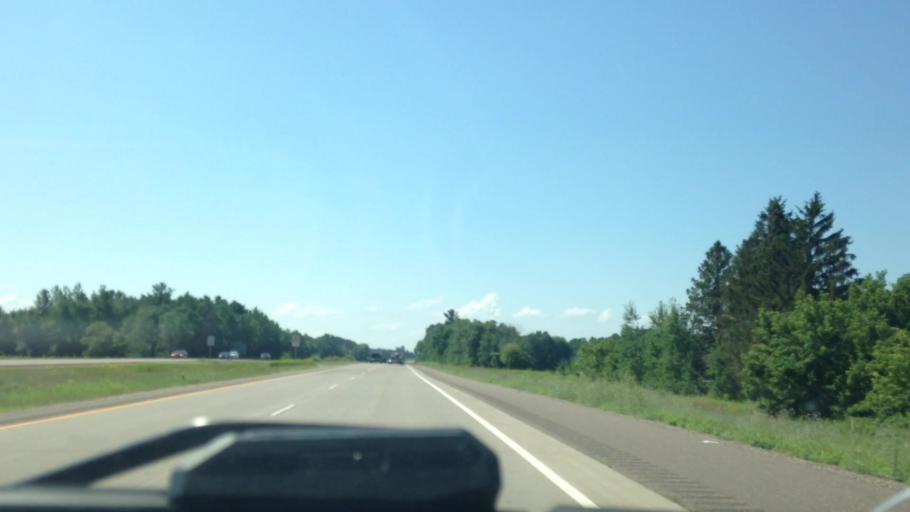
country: US
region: Wisconsin
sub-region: Barron County
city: Cameron
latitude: 45.4531
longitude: -91.7603
